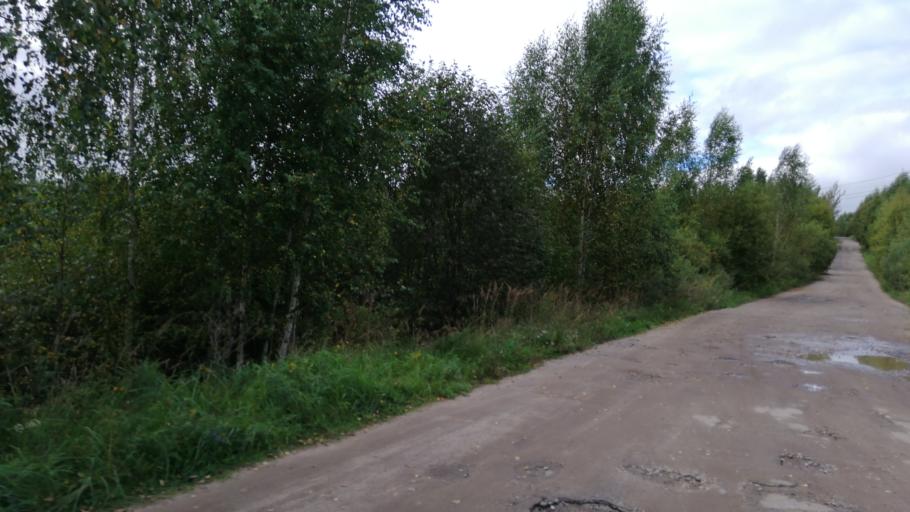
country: RU
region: Jaroslavl
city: Konstantinovskiy
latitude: 57.7999
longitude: 39.7180
